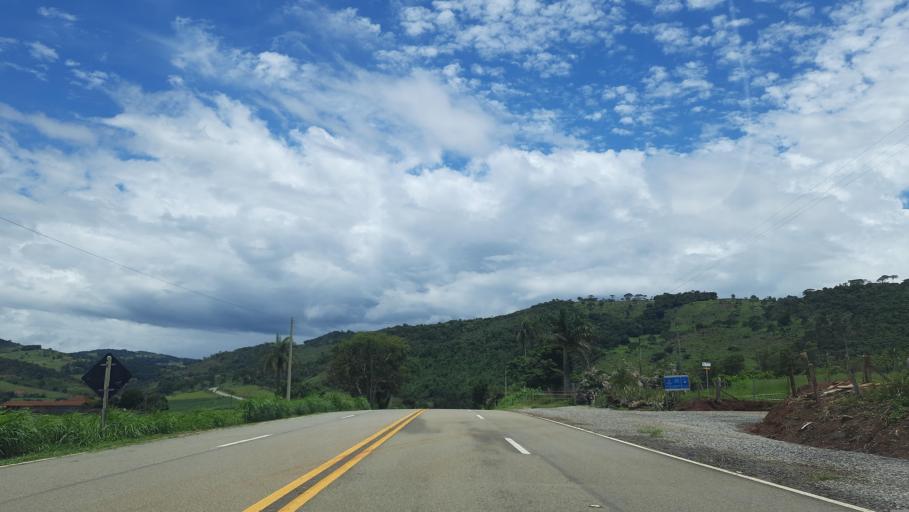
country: BR
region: Sao Paulo
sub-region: Vargem Grande Do Sul
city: Vargem Grande do Sul
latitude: -21.8246
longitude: -46.7797
